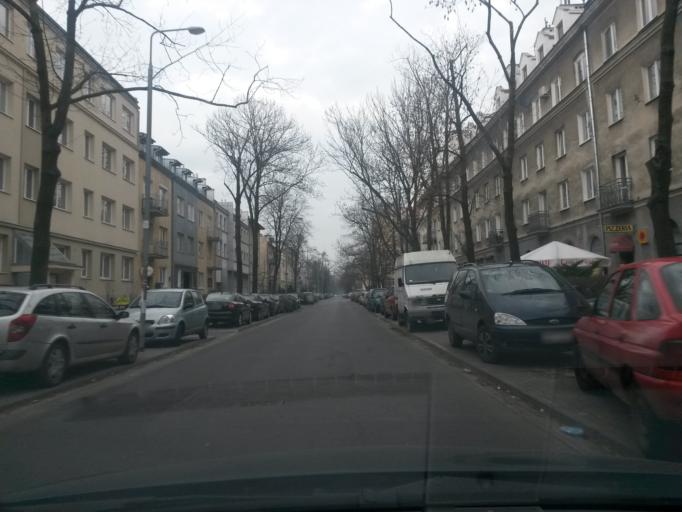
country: PL
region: Masovian Voivodeship
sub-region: Warszawa
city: Mokotow
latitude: 52.2032
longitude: 21.0379
